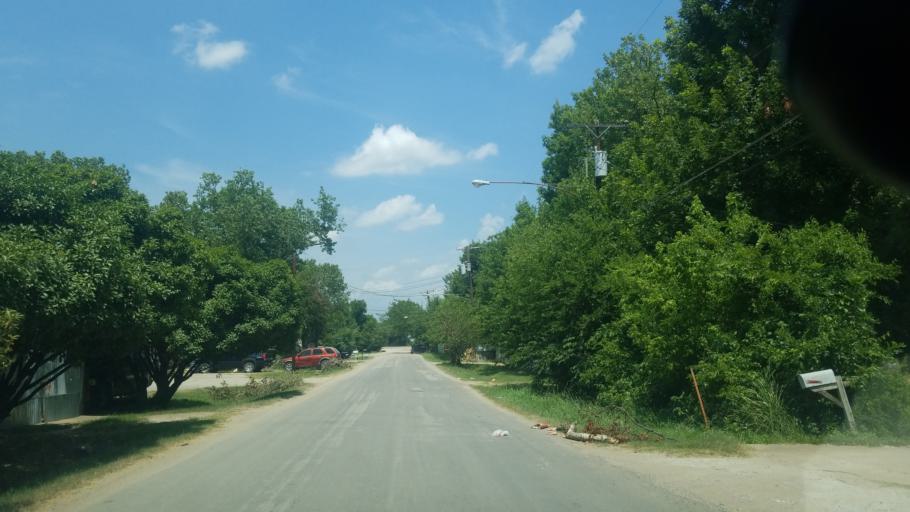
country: US
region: Texas
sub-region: Dallas County
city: Dallas
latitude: 32.7156
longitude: -96.7637
